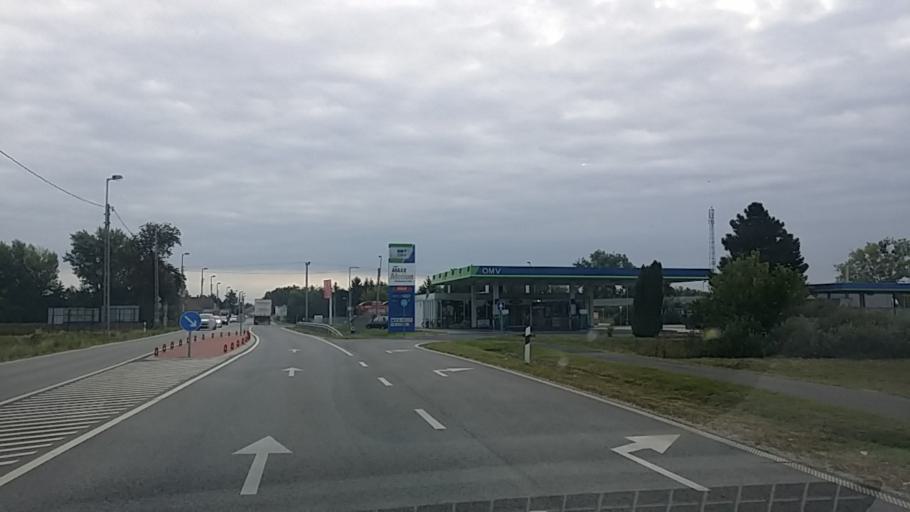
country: HU
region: Gyor-Moson-Sopron
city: Kapuvar
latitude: 47.5899
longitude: 17.0085
